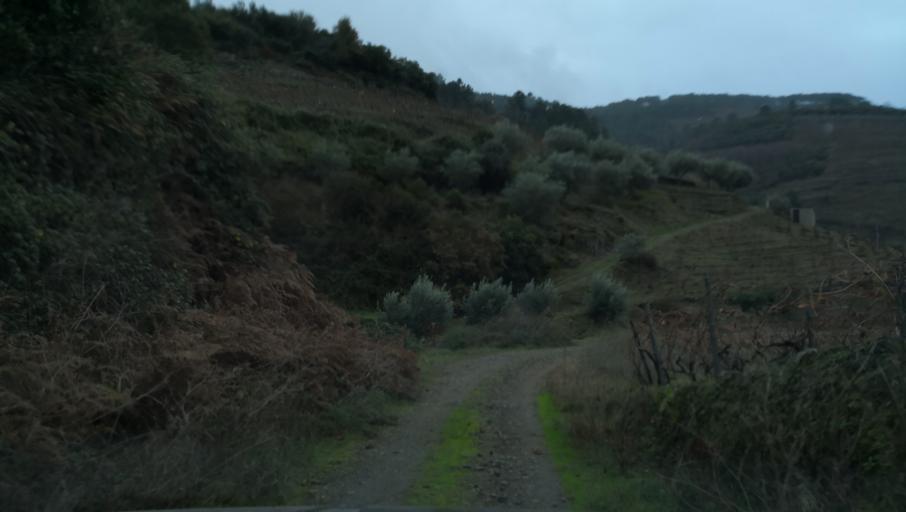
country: PT
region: Vila Real
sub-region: Santa Marta de Penaguiao
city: Santa Marta de Penaguiao
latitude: 41.2282
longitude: -7.7408
